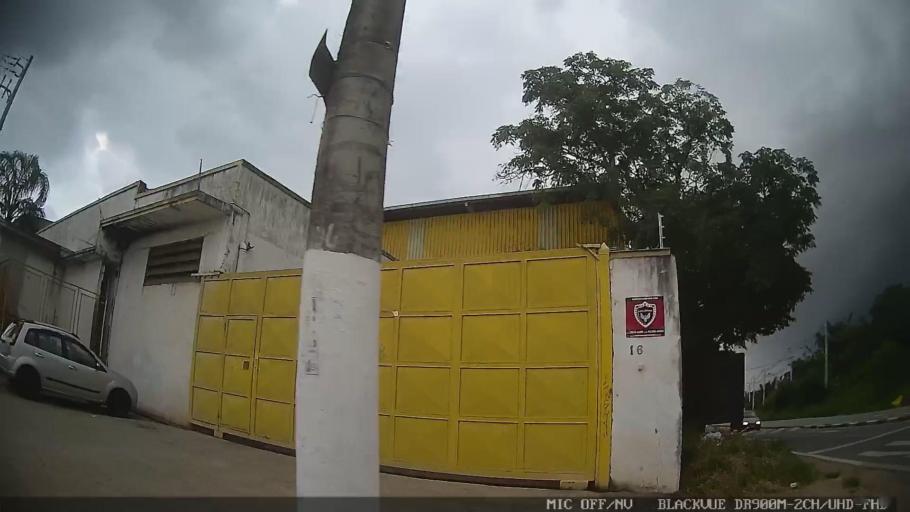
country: BR
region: Sao Paulo
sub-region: Suzano
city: Suzano
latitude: -23.6251
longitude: -46.3006
